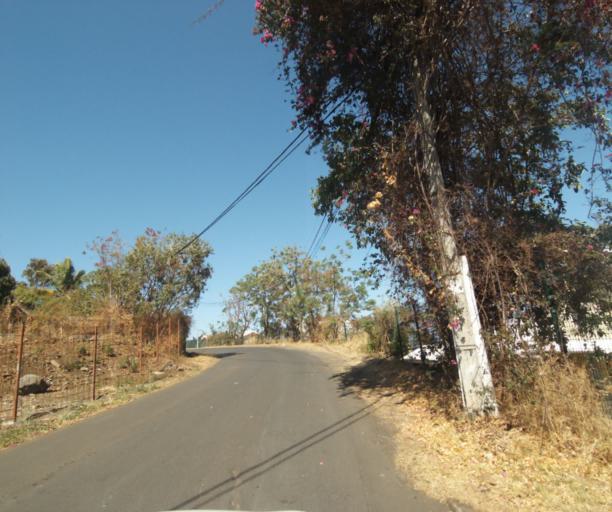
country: RE
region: Reunion
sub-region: Reunion
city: Saint-Paul
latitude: -20.9885
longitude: 55.3242
